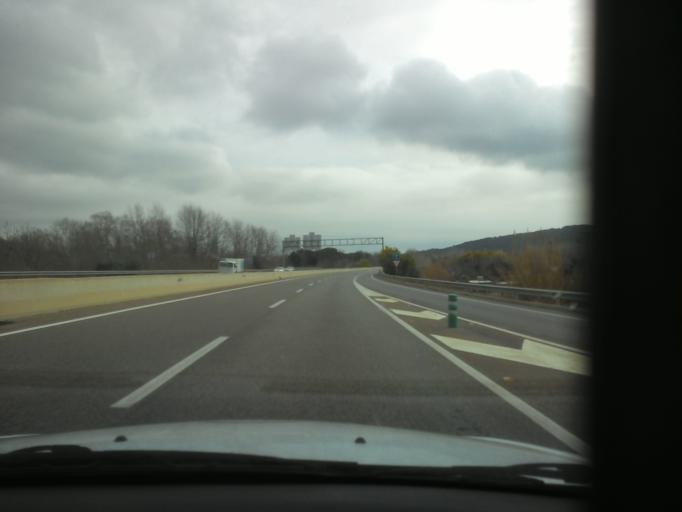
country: ES
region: Catalonia
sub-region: Provincia de Girona
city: Santa Cristina d'Aro
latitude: 41.8086
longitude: 3.0060
